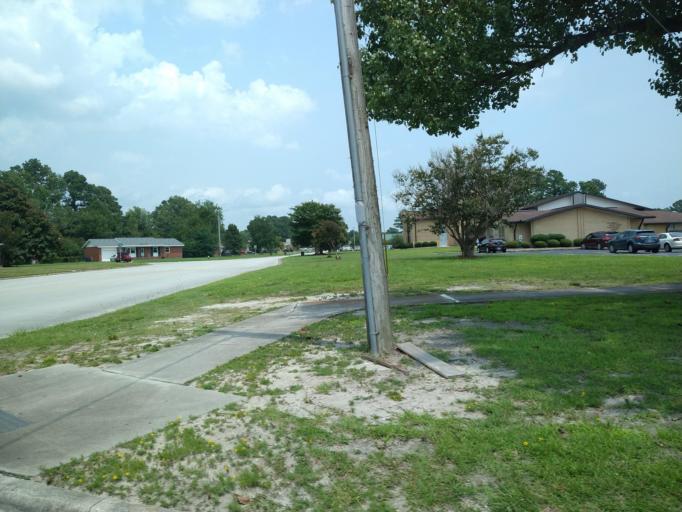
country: US
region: North Carolina
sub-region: Onslow County
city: Pumpkin Center
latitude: 34.7490
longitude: -77.3799
